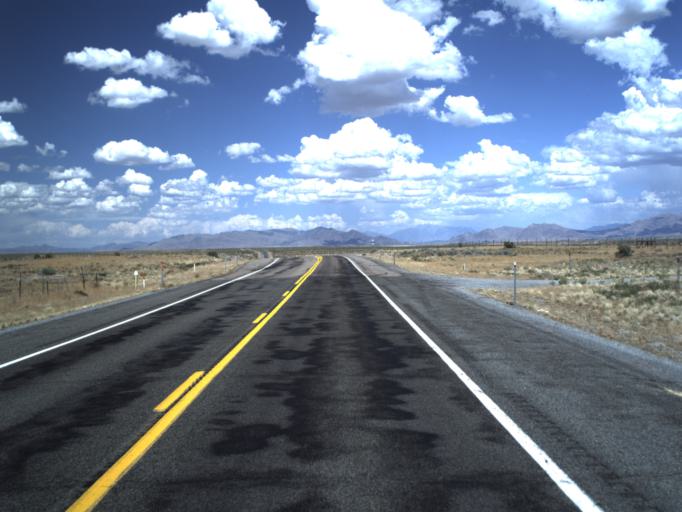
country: US
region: Utah
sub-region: Millard County
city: Delta
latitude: 39.3930
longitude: -112.5083
